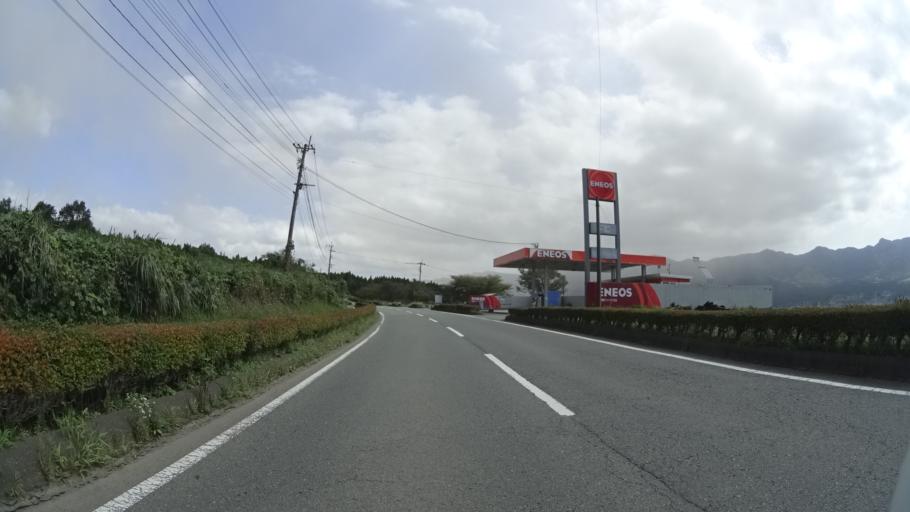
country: JP
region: Kumamoto
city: Aso
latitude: 32.8410
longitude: 131.0481
